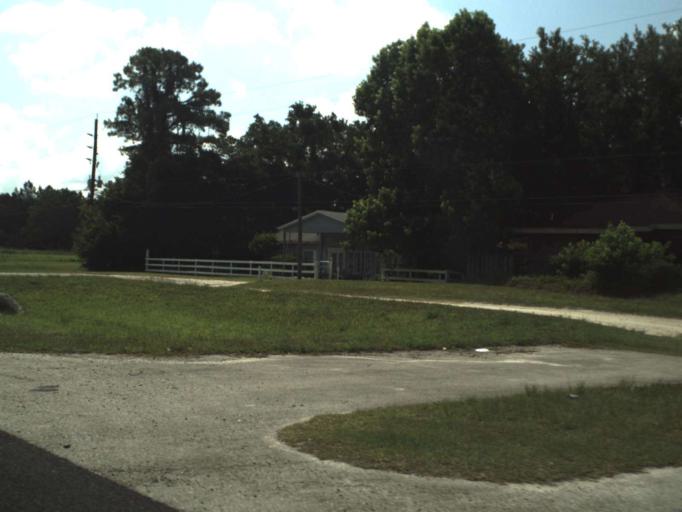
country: US
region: Florida
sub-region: Volusia County
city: Samsula-Spruce Creek
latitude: 29.0113
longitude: -81.0550
